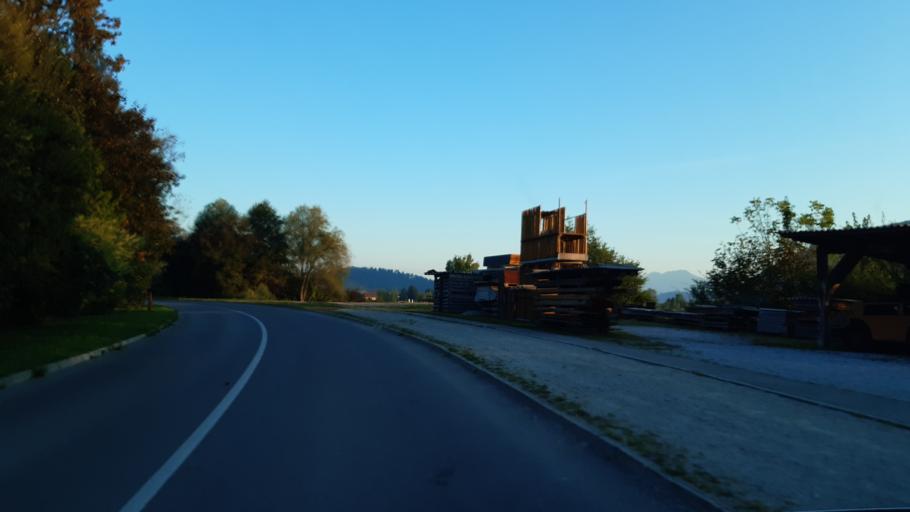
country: SI
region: Medvode
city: Zgornje Pirnice
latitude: 46.1050
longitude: 14.4438
